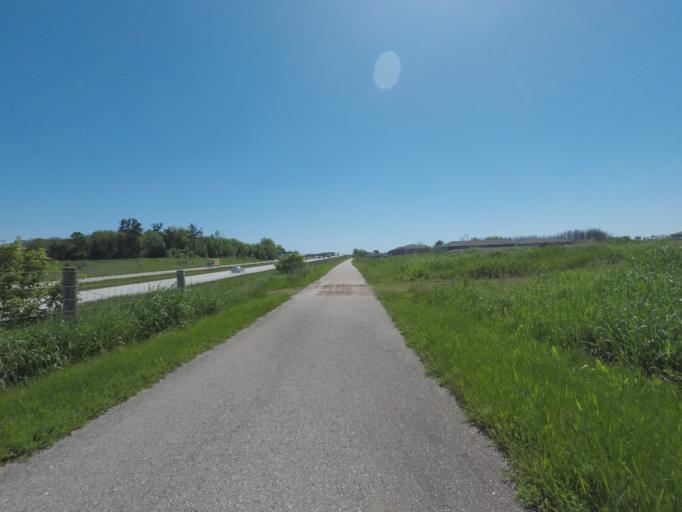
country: US
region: Wisconsin
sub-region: Sheboygan County
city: Sheboygan Falls
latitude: 43.7504
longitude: -87.8325
